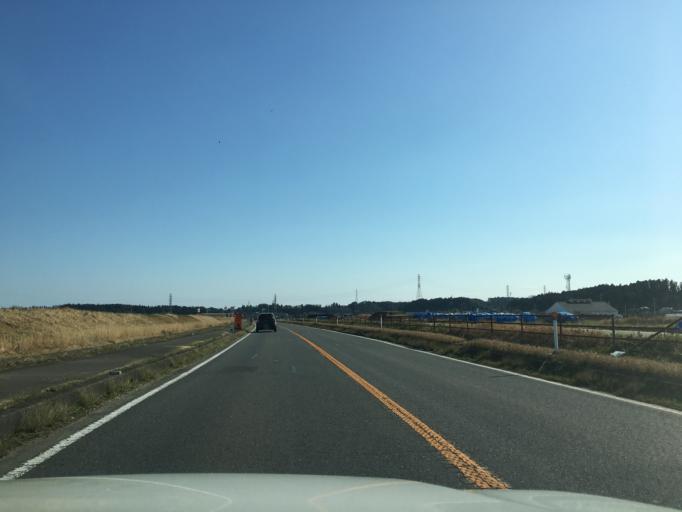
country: JP
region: Ibaraki
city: Mito-shi
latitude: 36.4282
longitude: 140.4211
